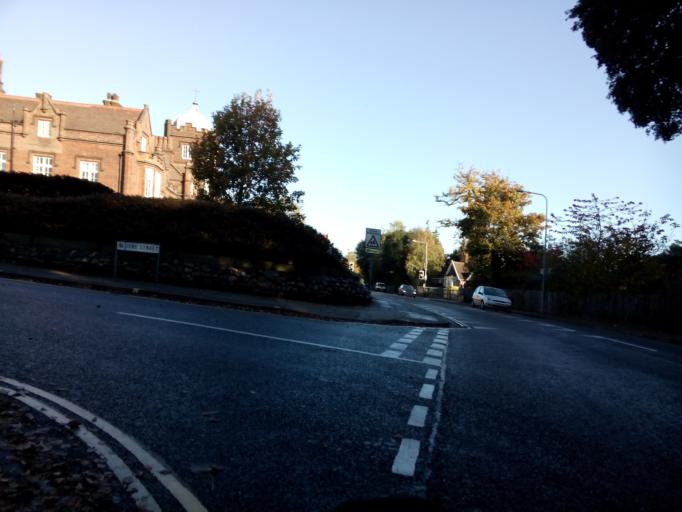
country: GB
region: England
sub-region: Suffolk
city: Ipswich
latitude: 52.0635
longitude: 1.1519
